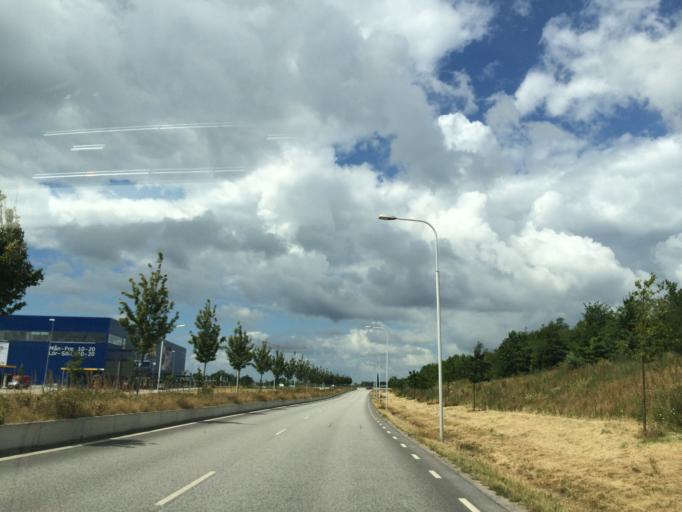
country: SE
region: Skane
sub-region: Malmo
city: Tygelsjo
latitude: 55.5541
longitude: 12.9893
